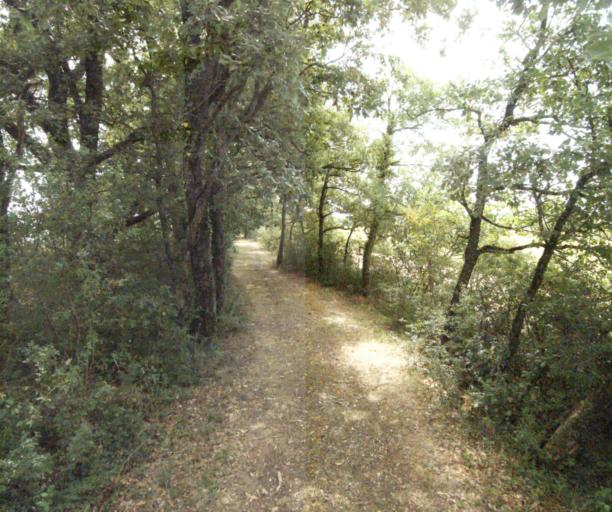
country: FR
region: Midi-Pyrenees
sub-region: Departement de la Haute-Garonne
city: Saint-Felix-Lauragais
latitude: 43.4271
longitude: 1.9247
